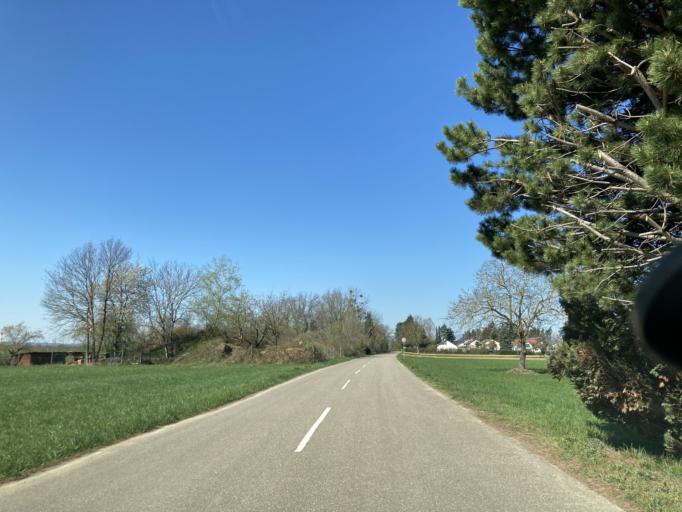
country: DE
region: Baden-Wuerttemberg
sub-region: Freiburg Region
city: Schliengen
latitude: 47.7632
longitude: 7.5619
